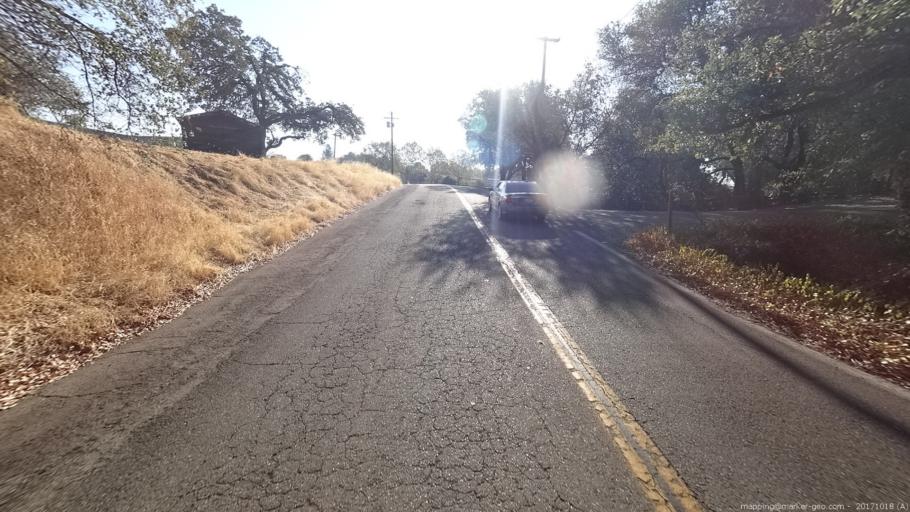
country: US
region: California
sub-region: Shasta County
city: Redding
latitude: 40.5622
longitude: -122.3644
